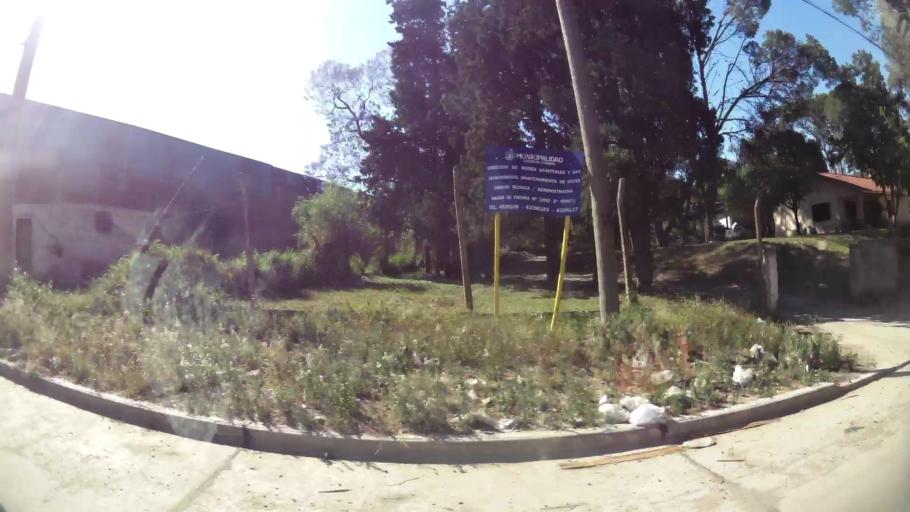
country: AR
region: Cordoba
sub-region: Departamento de Capital
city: Cordoba
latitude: -31.4076
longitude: -64.1496
